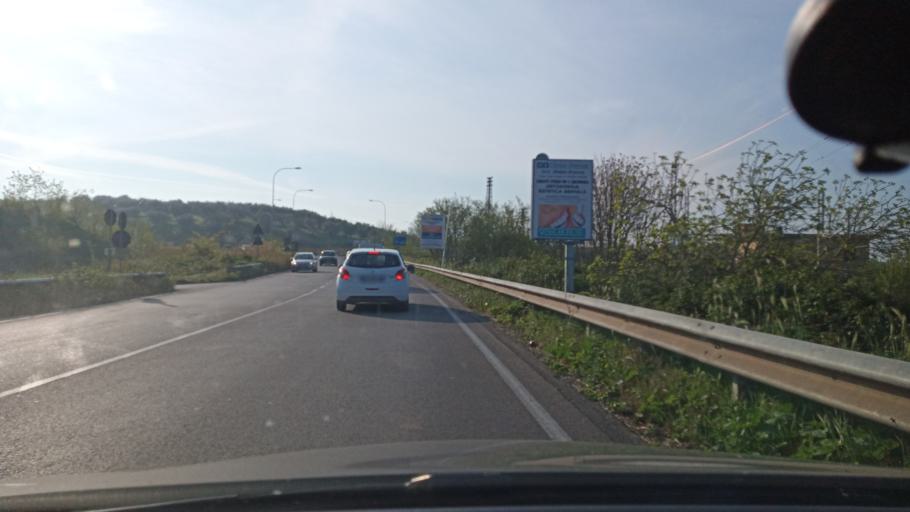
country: IT
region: Latium
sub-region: Citta metropolitana di Roma Capitale
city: Fiano Romano
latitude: 42.1636
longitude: 12.6455
